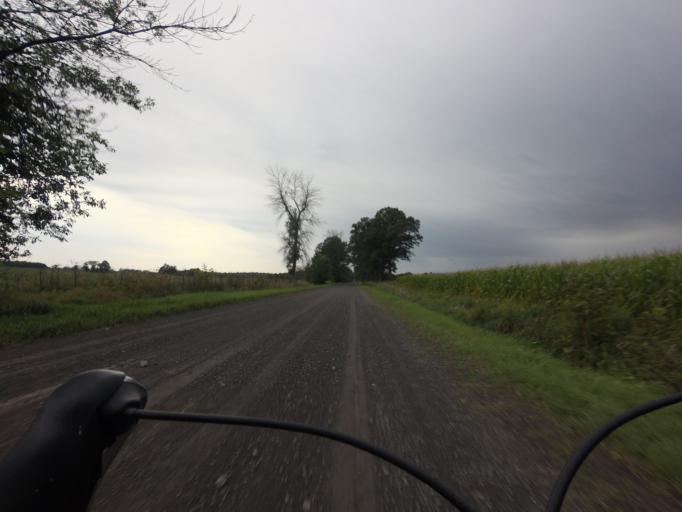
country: CA
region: Ontario
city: Bells Corners
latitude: 45.1610
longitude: -75.6964
